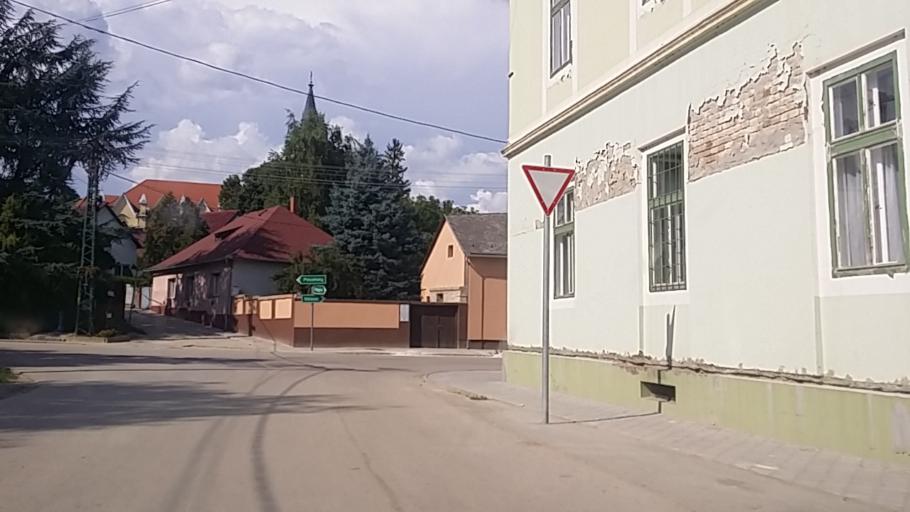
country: HU
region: Tolna
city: Gyonk
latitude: 46.5552
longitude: 18.4773
